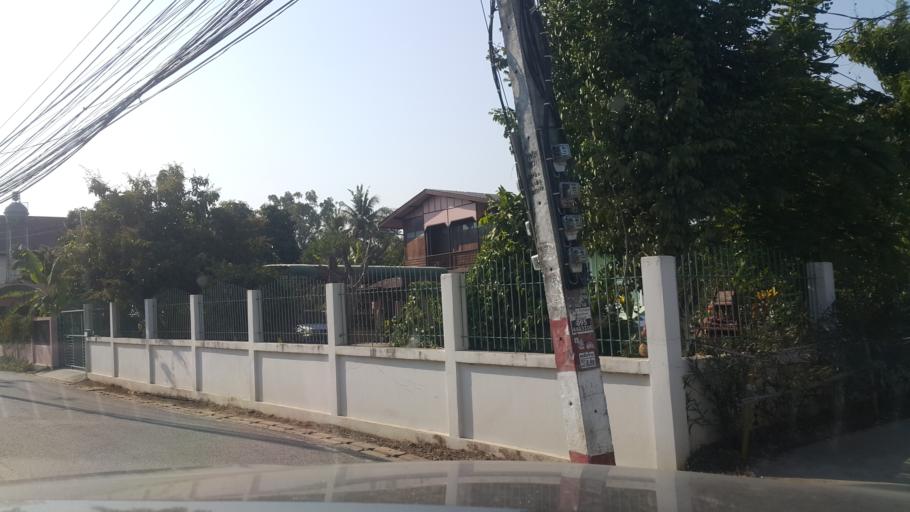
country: TH
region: Chiang Mai
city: Saraphi
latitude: 18.7348
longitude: 99.0271
